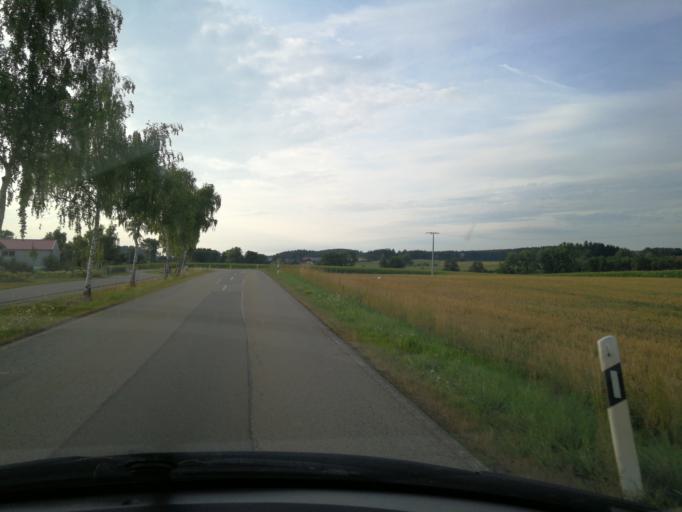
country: DE
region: Bavaria
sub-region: Lower Bavaria
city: Wiesenfelden
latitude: 49.0464
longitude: 12.5328
